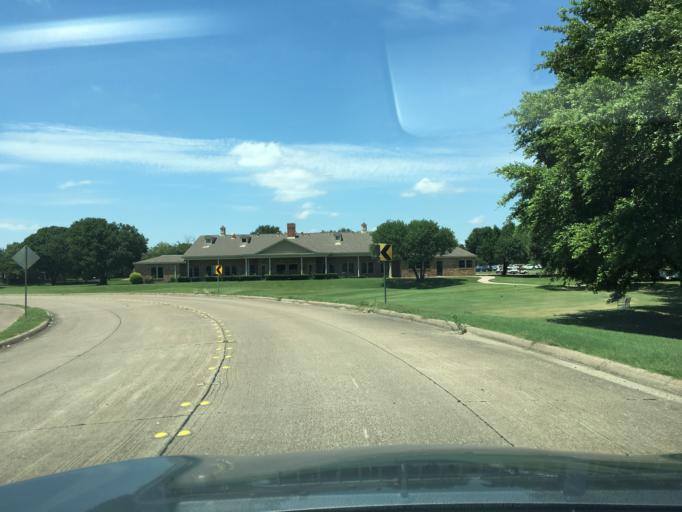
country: US
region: Texas
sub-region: Dallas County
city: Garland
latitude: 32.9392
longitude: -96.6736
